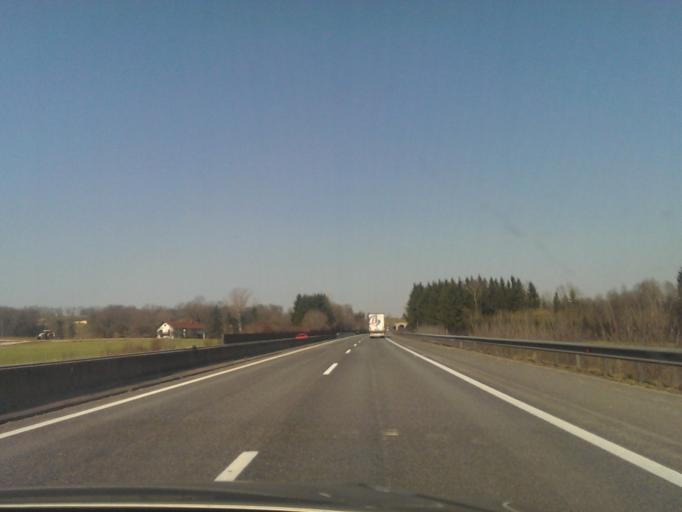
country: AT
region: Upper Austria
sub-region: Politischer Bezirk Kirchdorf an der Krems
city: Kremsmunster
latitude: 47.9655
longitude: 14.0961
